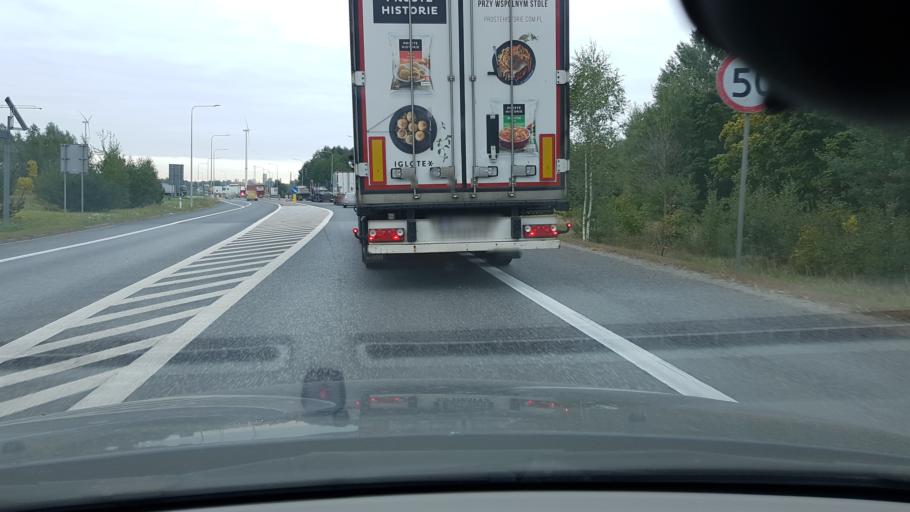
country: PL
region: Masovian Voivodeship
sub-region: Powiat zyrardowski
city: Mszczonow
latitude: 51.9939
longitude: 20.5000
